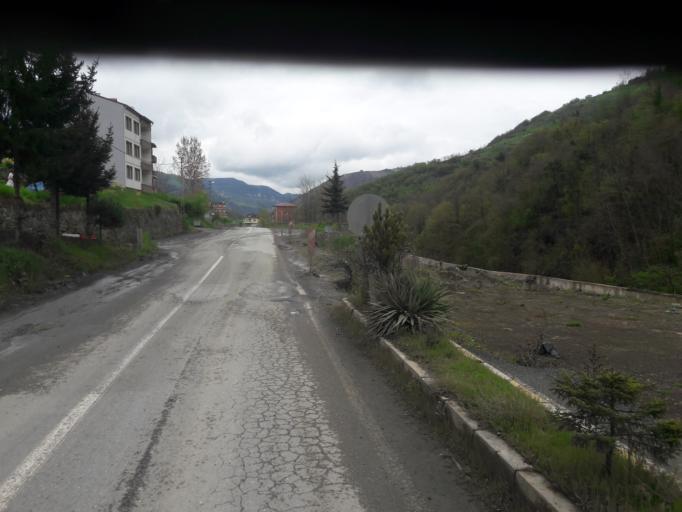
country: TR
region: Trabzon
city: Duzkoy
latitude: 40.9281
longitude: 39.4939
